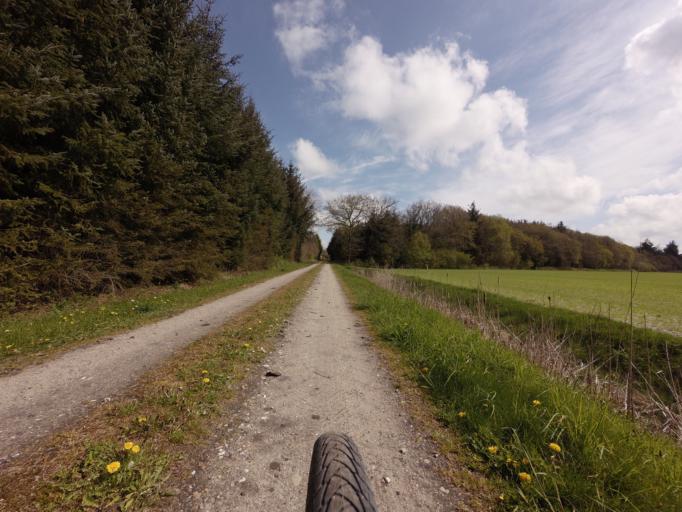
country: DK
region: North Denmark
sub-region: Jammerbugt Kommune
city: Kas
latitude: 57.1992
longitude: 9.5998
